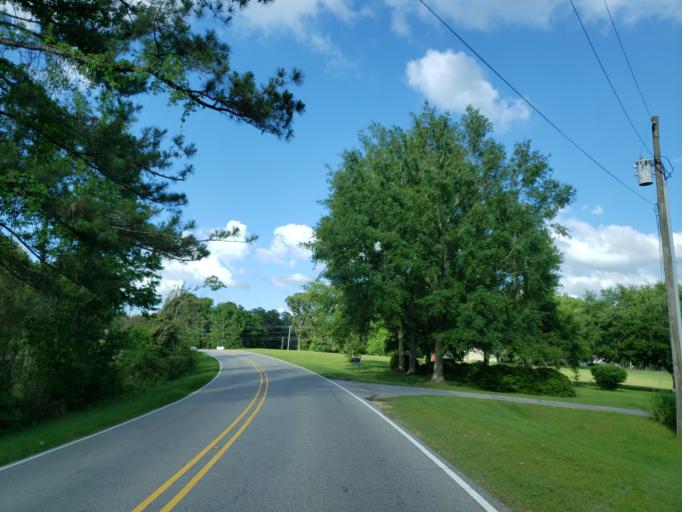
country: US
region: Mississippi
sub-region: Lamar County
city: West Hattiesburg
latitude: 31.2808
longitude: -89.4304
